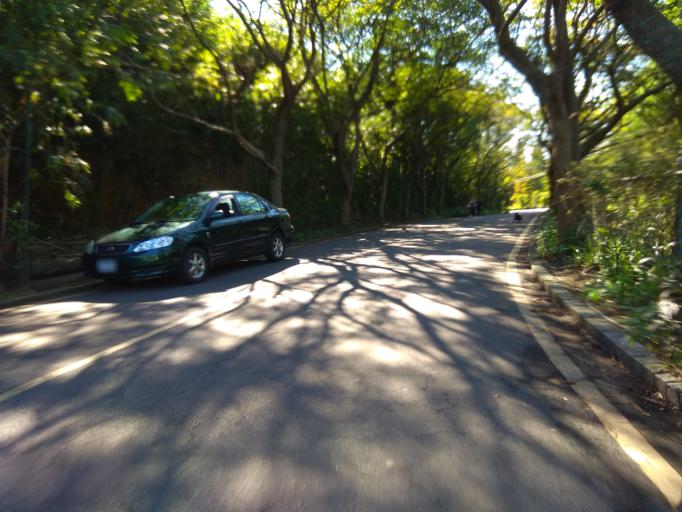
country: TW
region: Taiwan
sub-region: Hsinchu
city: Zhubei
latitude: 24.8602
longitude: 121.1048
